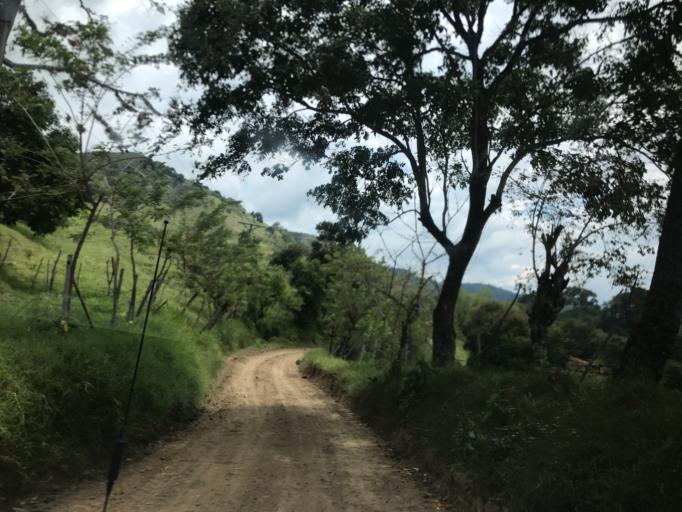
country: CO
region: Valle del Cauca
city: Obando
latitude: 4.5548
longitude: -75.9279
